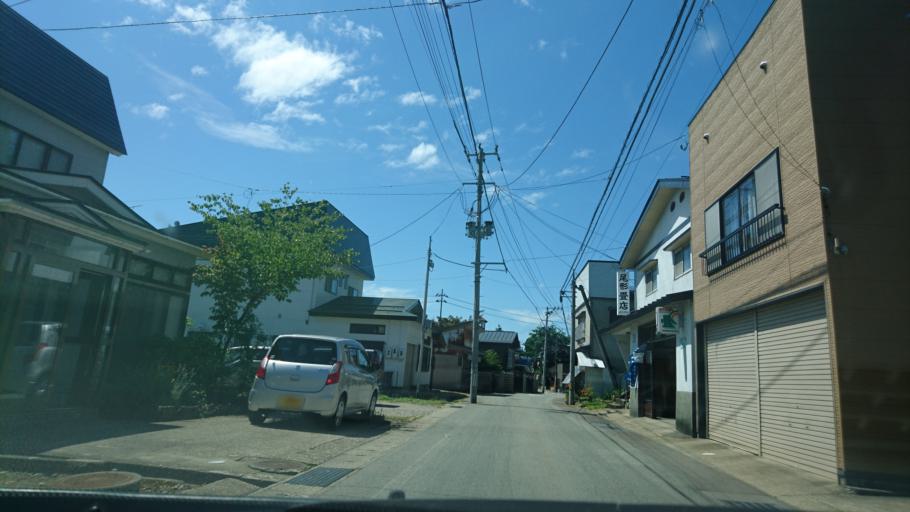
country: JP
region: Akita
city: Kakunodatemachi
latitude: 39.5868
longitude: 140.5640
